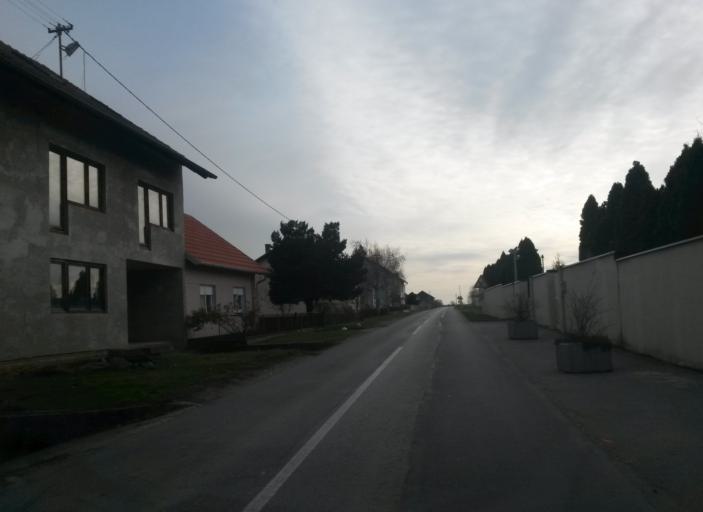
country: HR
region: Osjecko-Baranjska
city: Cepin
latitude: 45.5256
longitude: 18.5900
